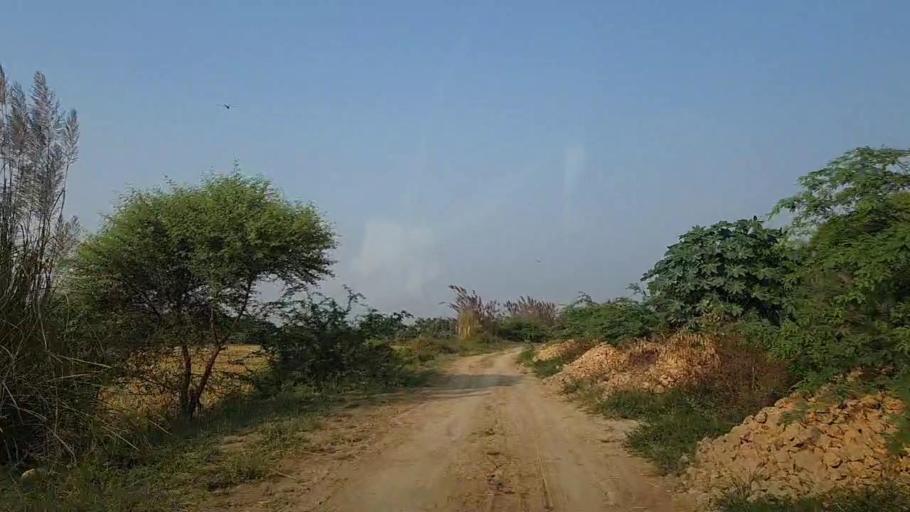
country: PK
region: Sindh
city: Thatta
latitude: 24.6606
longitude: 67.7720
